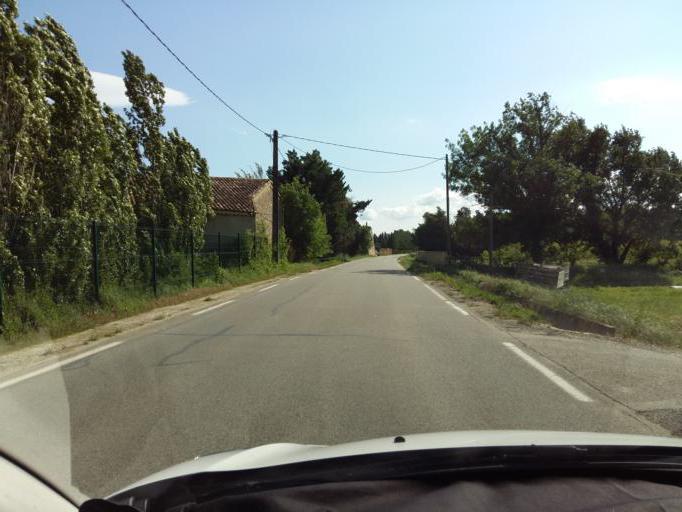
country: FR
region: Provence-Alpes-Cote d'Azur
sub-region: Departement du Vaucluse
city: Cavaillon
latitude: 43.8624
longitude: 5.0610
